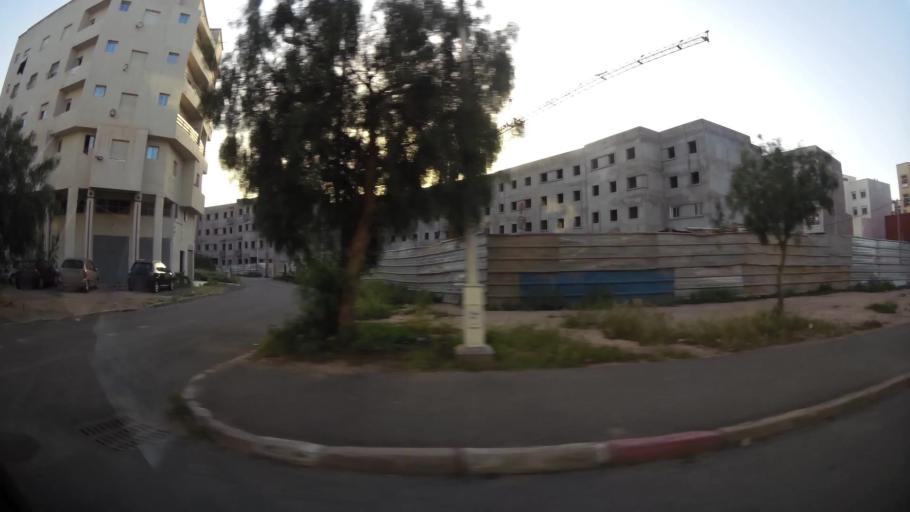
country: MA
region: Oued ed Dahab-Lagouira
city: Dakhla
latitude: 30.3939
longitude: -9.5656
